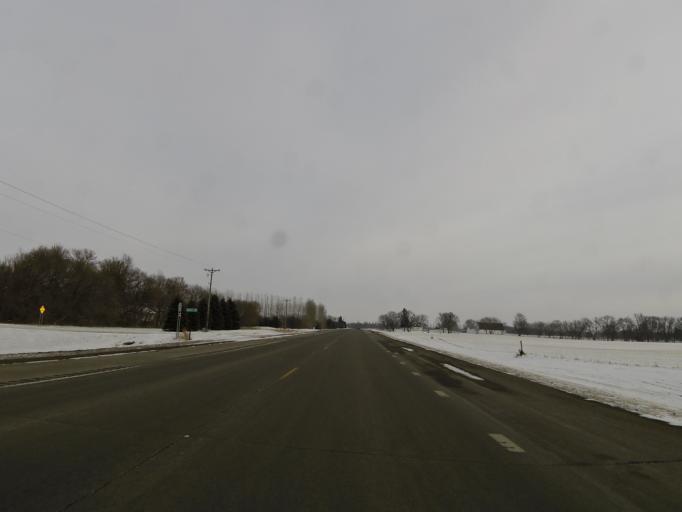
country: US
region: Minnesota
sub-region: McLeod County
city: Lester Prairie
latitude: 44.9063
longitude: -94.0907
